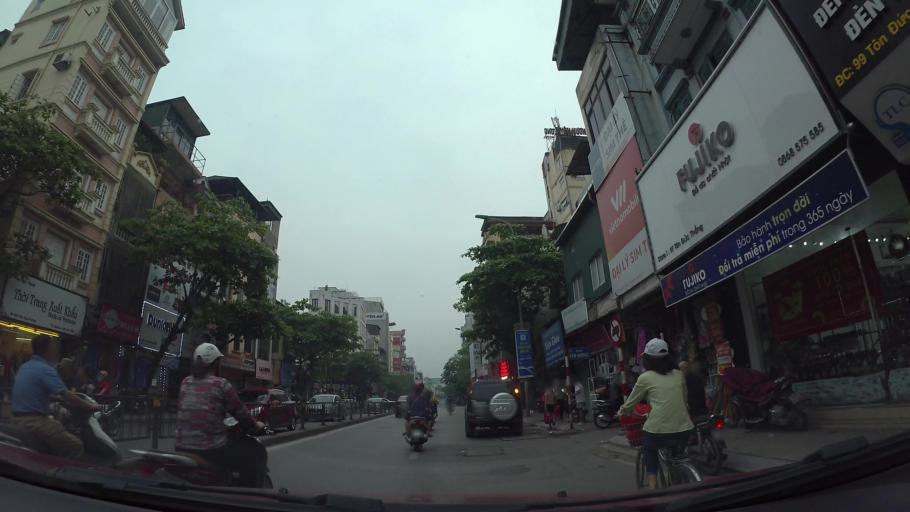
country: VN
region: Ha Noi
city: Dong Da
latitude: 21.0248
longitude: 105.8328
